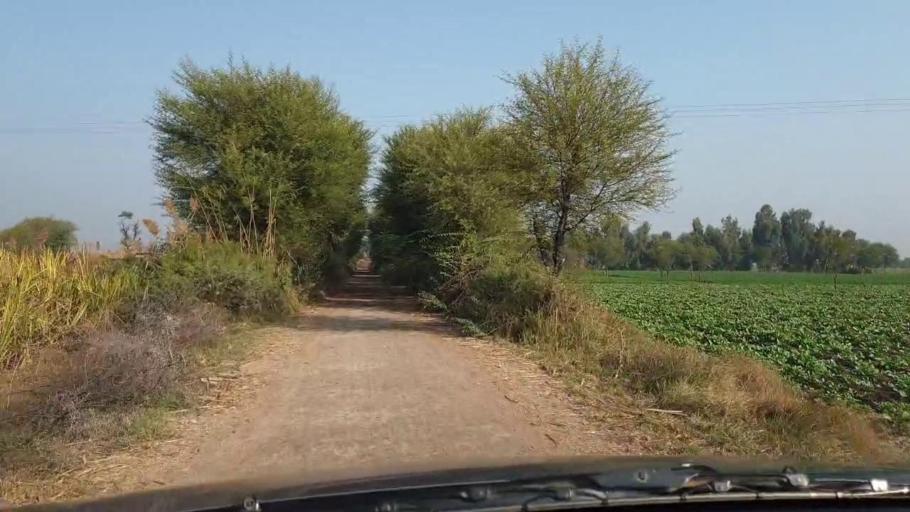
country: PK
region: Sindh
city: Sanghar
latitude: 25.9853
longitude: 68.9497
